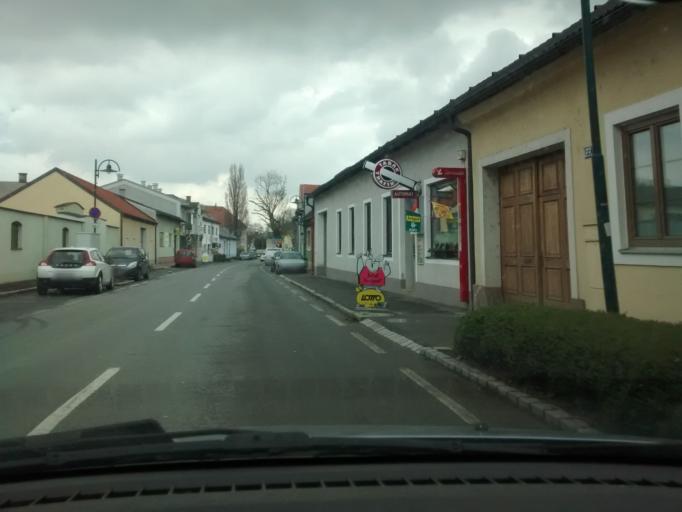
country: AT
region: Lower Austria
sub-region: Politischer Bezirk Modling
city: Biedermannsdorf
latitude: 48.0843
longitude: 16.3411
